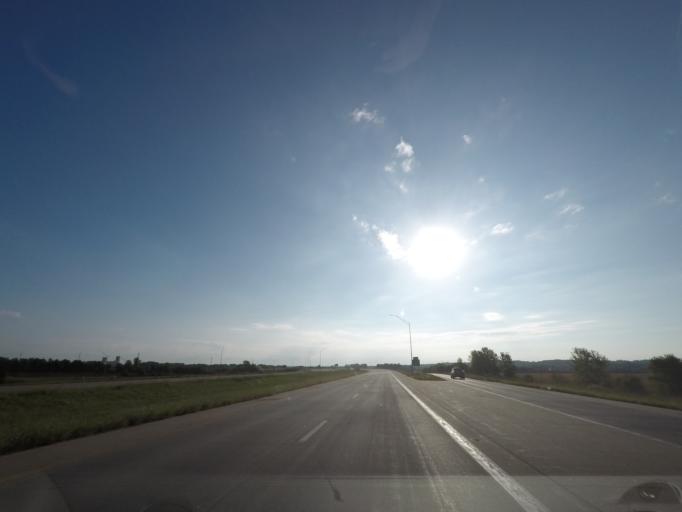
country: US
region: Iowa
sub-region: Warren County
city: Carlisle
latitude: 41.5113
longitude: -93.5306
